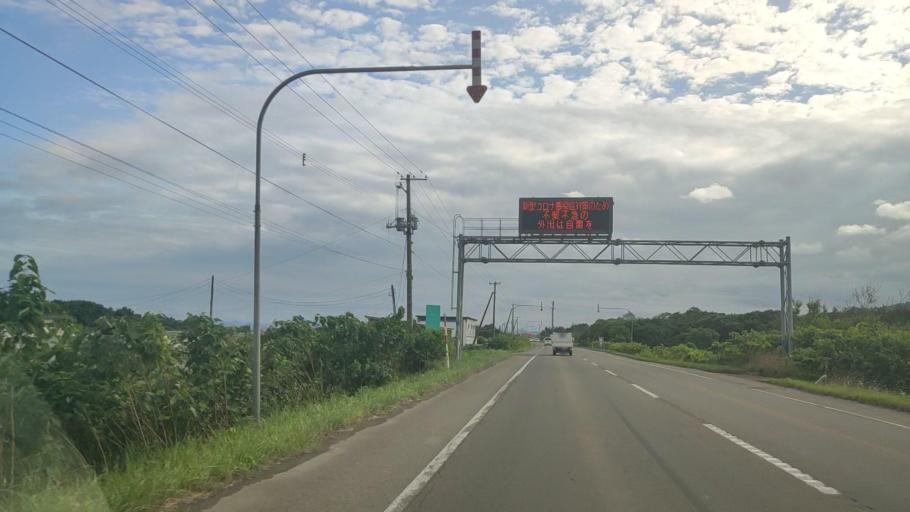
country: JP
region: Hokkaido
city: Niseko Town
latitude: 42.4855
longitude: 140.3538
